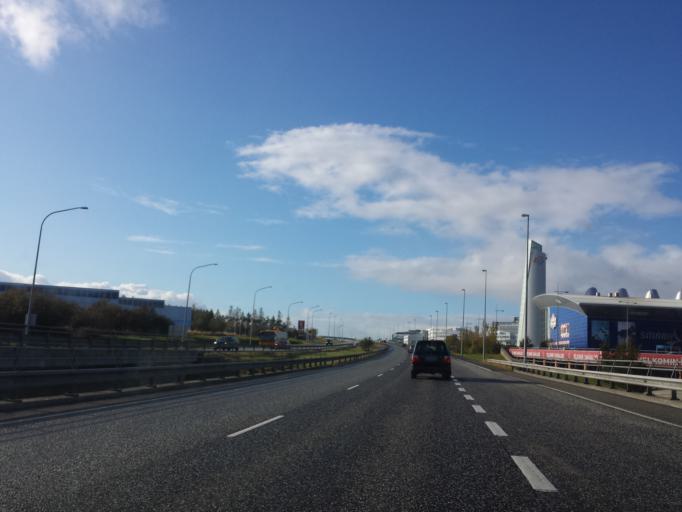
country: IS
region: Capital Region
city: Kopavogur
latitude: 64.1016
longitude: -21.8782
